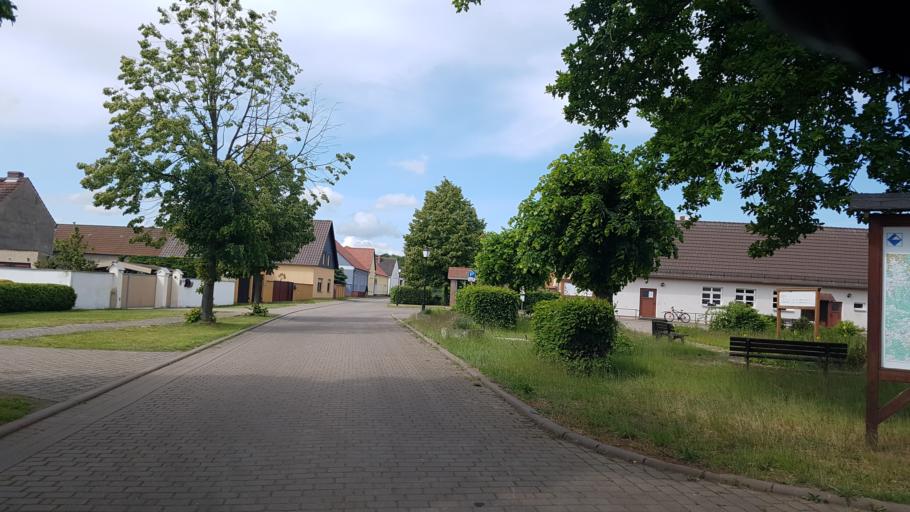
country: DE
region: Brandenburg
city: Luckau
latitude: 51.8188
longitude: 13.6973
